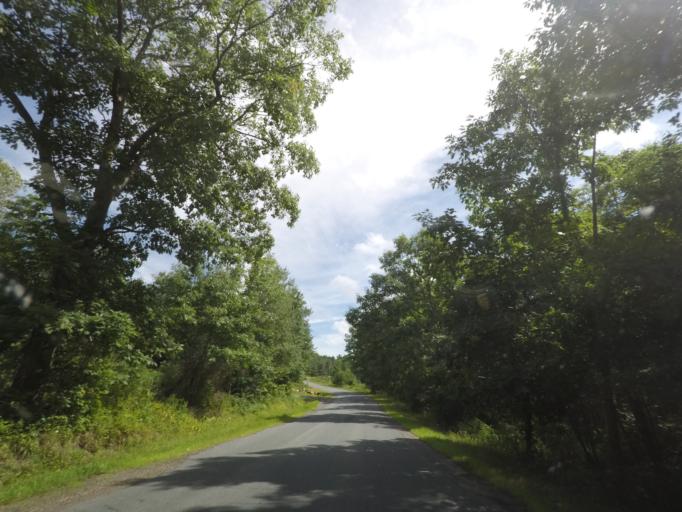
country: US
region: New York
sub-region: Rensselaer County
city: Poestenkill
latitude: 42.6750
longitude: -73.5510
